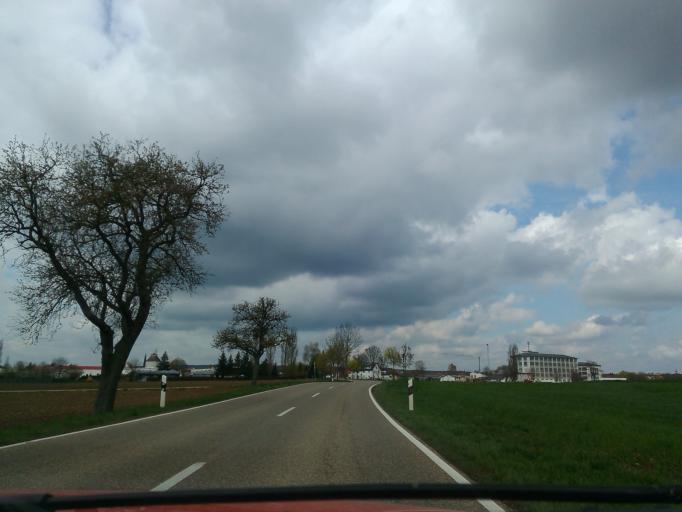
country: DE
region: Baden-Wuerttemberg
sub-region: Tuebingen Region
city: Langenau
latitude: 48.4903
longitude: 10.1337
